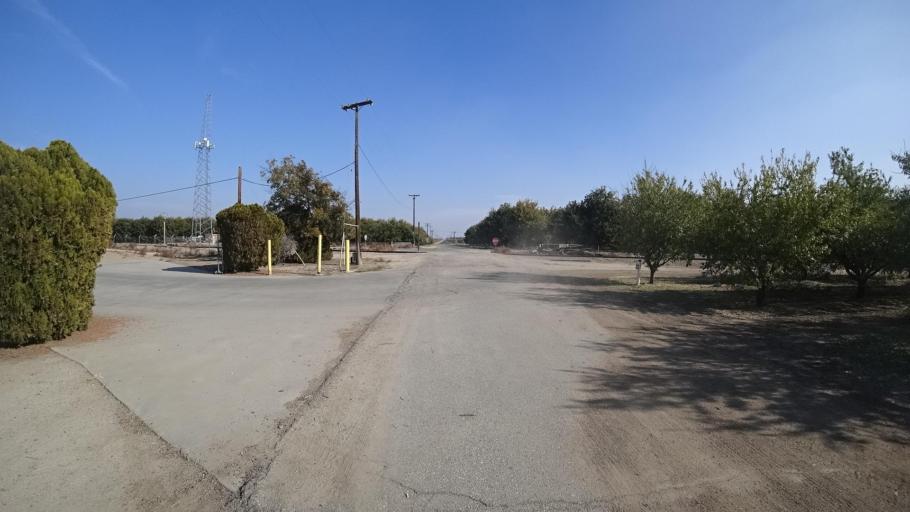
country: US
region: California
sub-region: Kern County
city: McFarland
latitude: 35.6311
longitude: -119.2074
